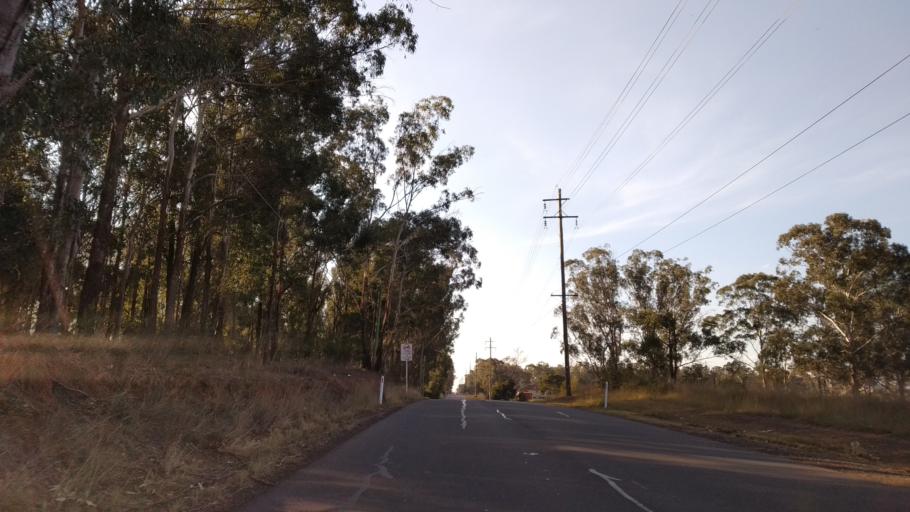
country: AU
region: New South Wales
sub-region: Penrith Municipality
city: Werrington Downs
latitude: -33.7104
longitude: 150.7318
